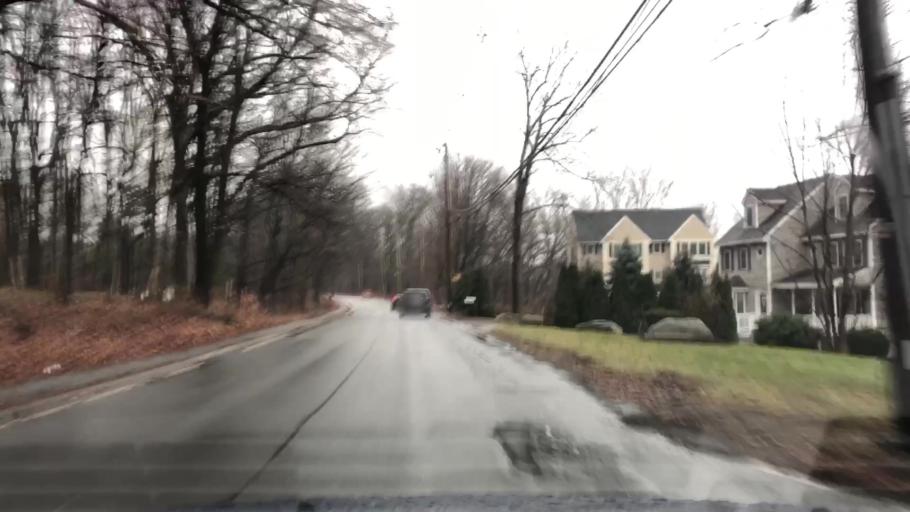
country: US
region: Massachusetts
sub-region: Essex County
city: North Andover
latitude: 42.6879
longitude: -71.1349
